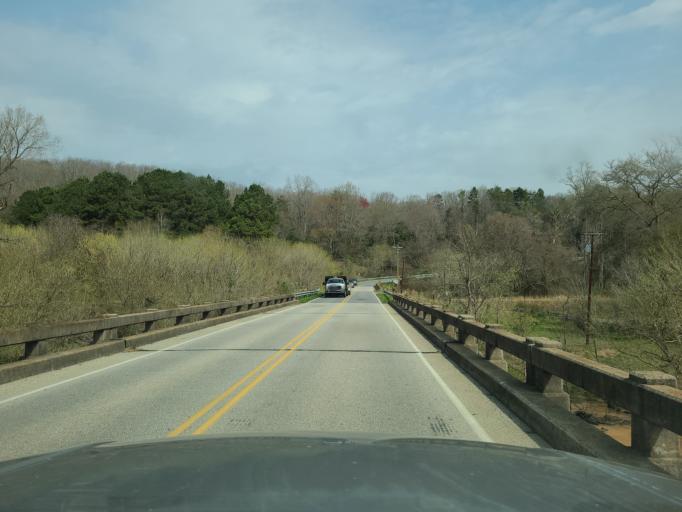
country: US
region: North Carolina
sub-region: Gaston County
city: Ranlo
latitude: 35.3085
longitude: -81.1068
